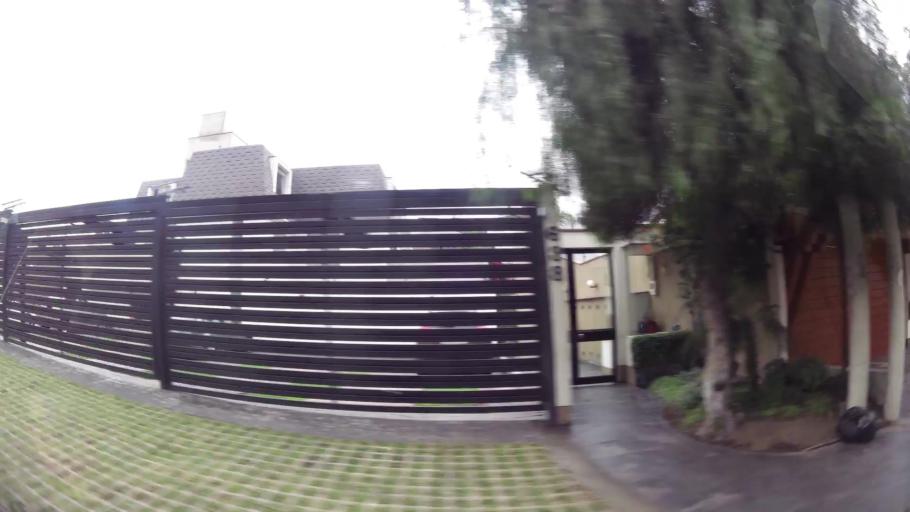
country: PE
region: Lima
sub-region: Lima
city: La Molina
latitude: -12.0782
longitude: -76.9189
